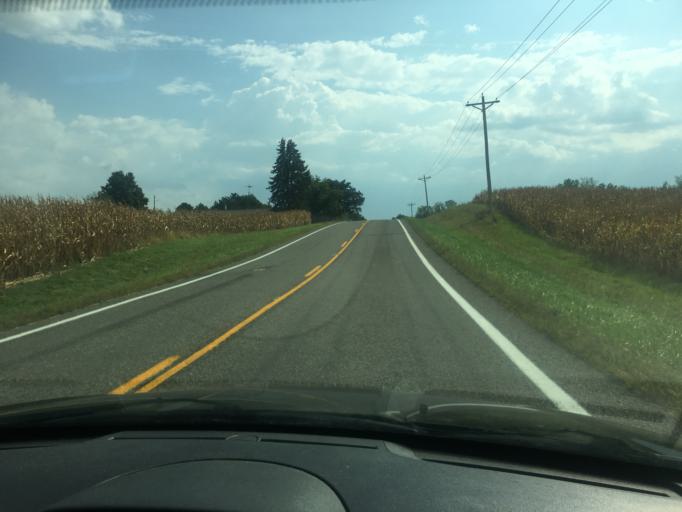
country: US
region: Ohio
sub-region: Champaign County
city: Urbana
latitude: 40.1511
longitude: -83.8337
